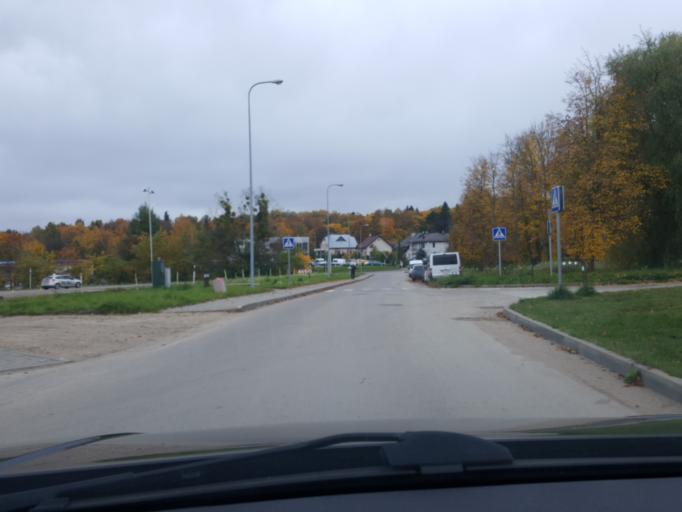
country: LT
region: Alytaus apskritis
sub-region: Alytus
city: Alytus
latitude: 54.3883
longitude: 24.0329
